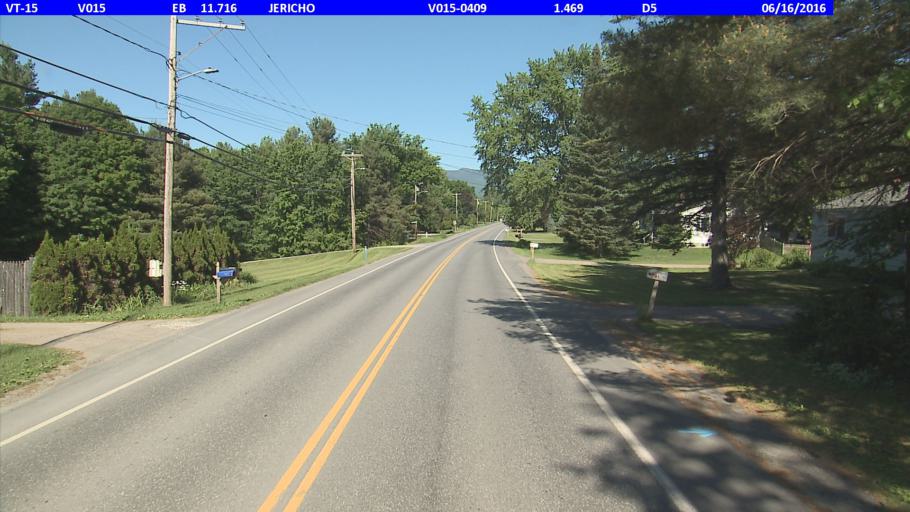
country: US
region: Vermont
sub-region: Chittenden County
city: Jericho
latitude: 44.5095
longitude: -72.9795
